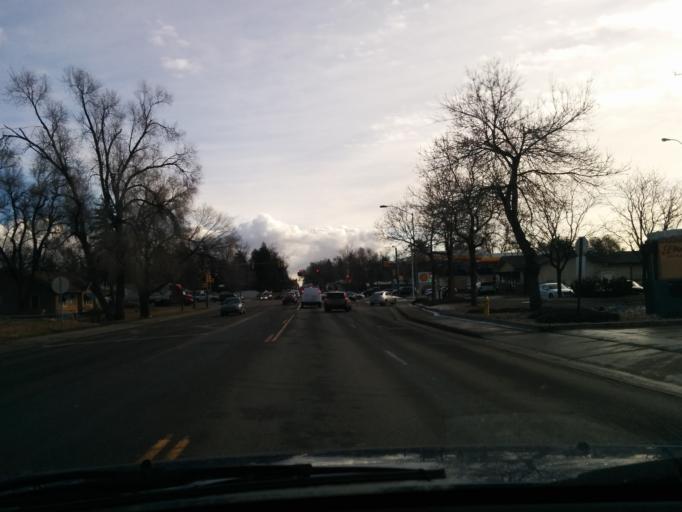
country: US
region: Colorado
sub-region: Larimer County
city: Fort Collins
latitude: 40.5671
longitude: -105.0784
